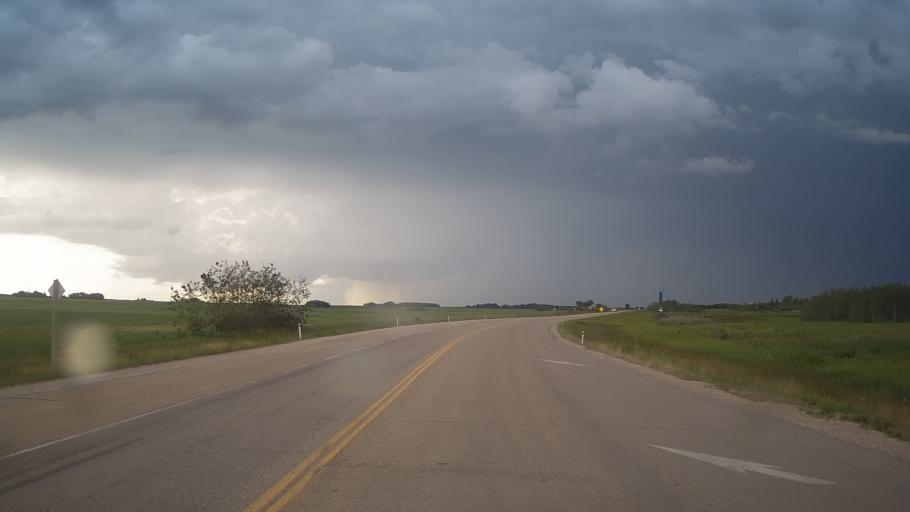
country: CA
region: Alberta
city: Tofield
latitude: 53.2833
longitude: -112.4172
